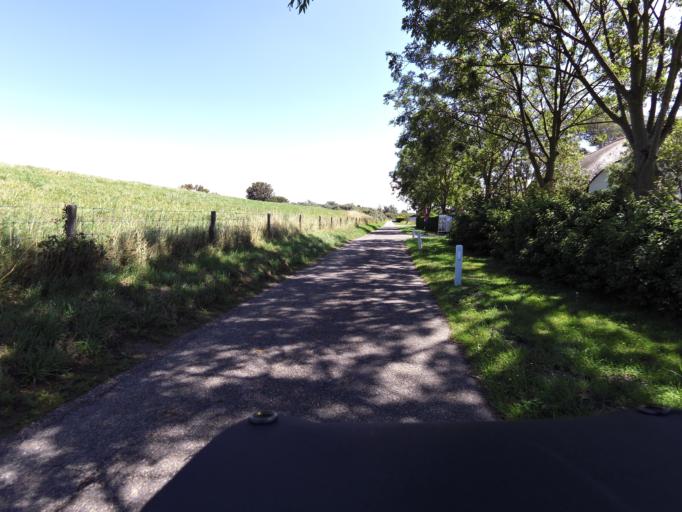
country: NL
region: South Holland
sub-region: Gemeente Goeree-Overflakkee
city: Goedereede
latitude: 51.8237
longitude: 4.0170
